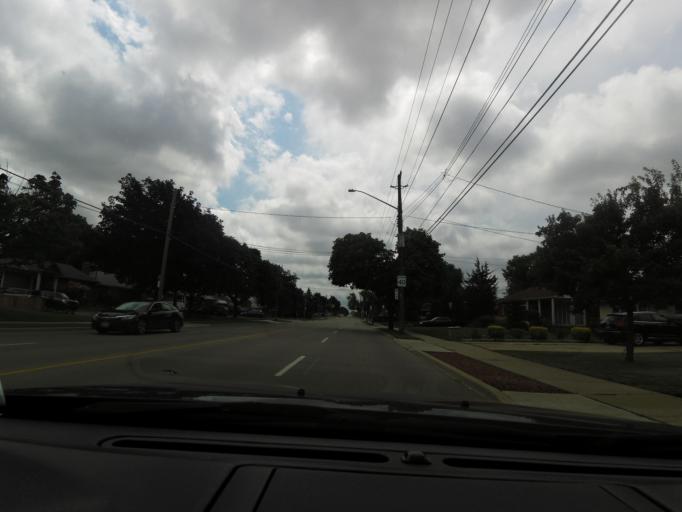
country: CA
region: Ontario
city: Hamilton
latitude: 43.2293
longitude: -79.8280
